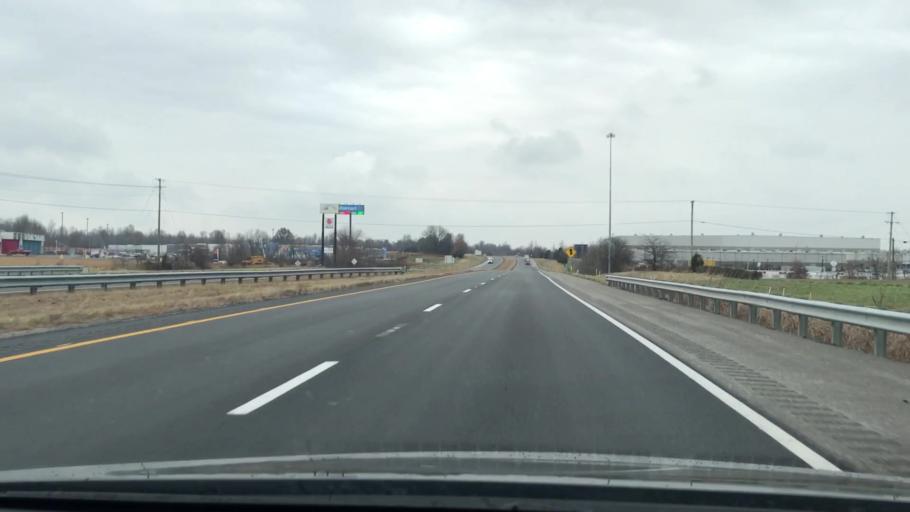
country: US
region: Kentucky
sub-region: Hopkins County
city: Madisonville
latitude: 37.4178
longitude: -87.4724
